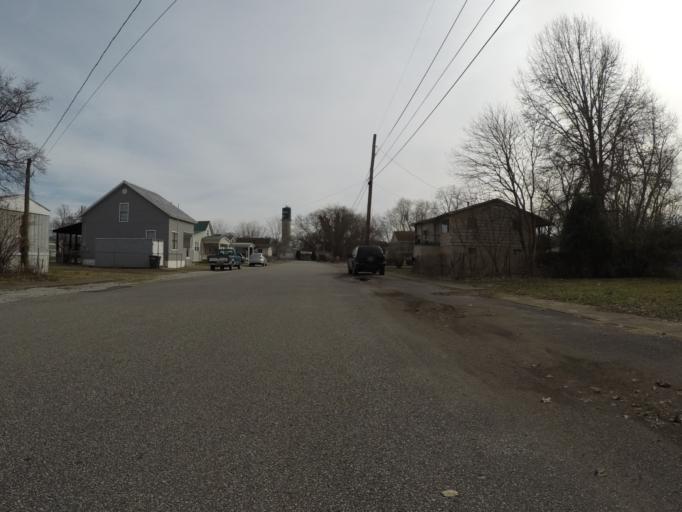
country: US
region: West Virginia
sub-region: Cabell County
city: Pea Ridge
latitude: 38.4364
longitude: -82.3810
